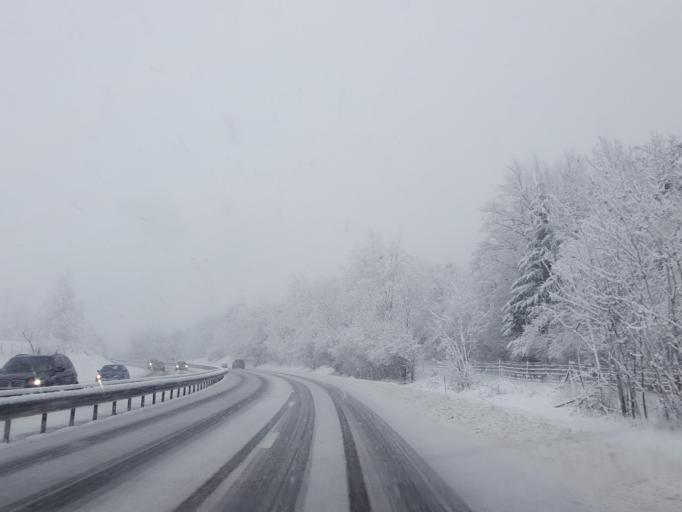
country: FR
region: Rhone-Alpes
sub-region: Departement de la Haute-Savoie
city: Groisy
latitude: 46.0121
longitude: 6.1973
